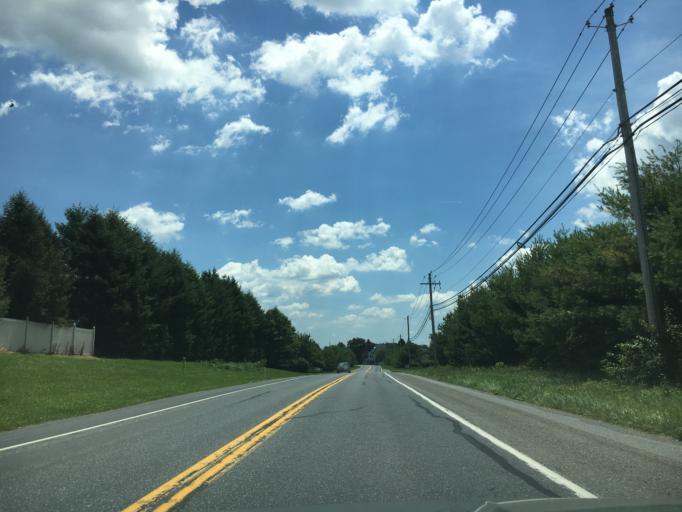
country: US
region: Pennsylvania
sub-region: Lehigh County
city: Schnecksville
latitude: 40.6934
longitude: -75.5911
